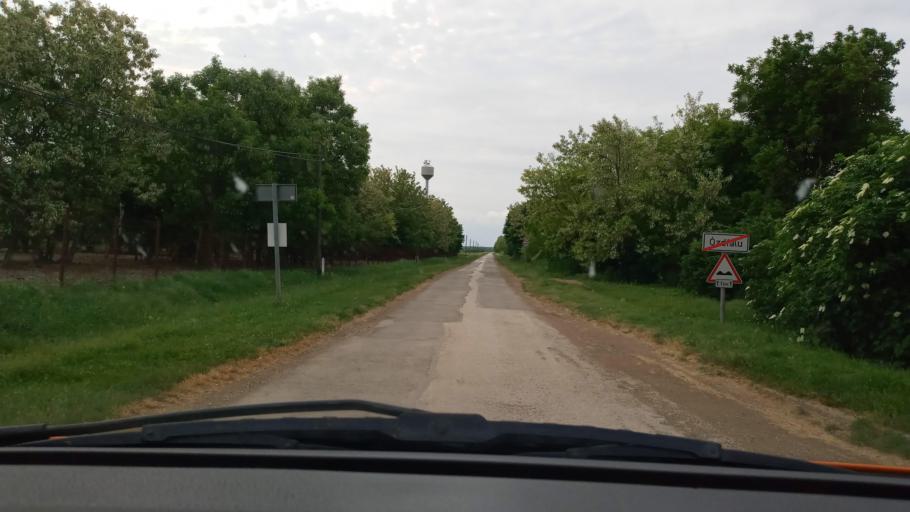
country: HU
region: Baranya
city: Vajszlo
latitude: 45.9286
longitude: 18.0219
